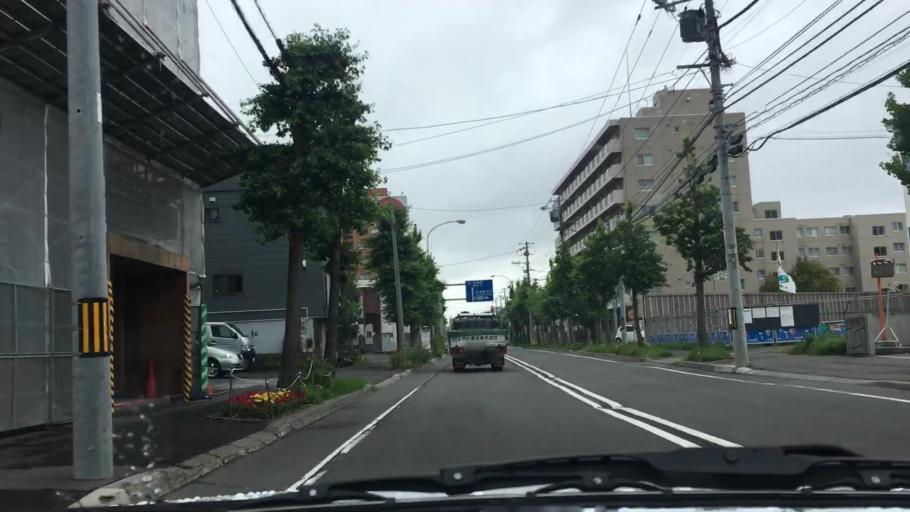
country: JP
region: Hokkaido
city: Sapporo
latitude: 43.0745
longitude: 141.3836
